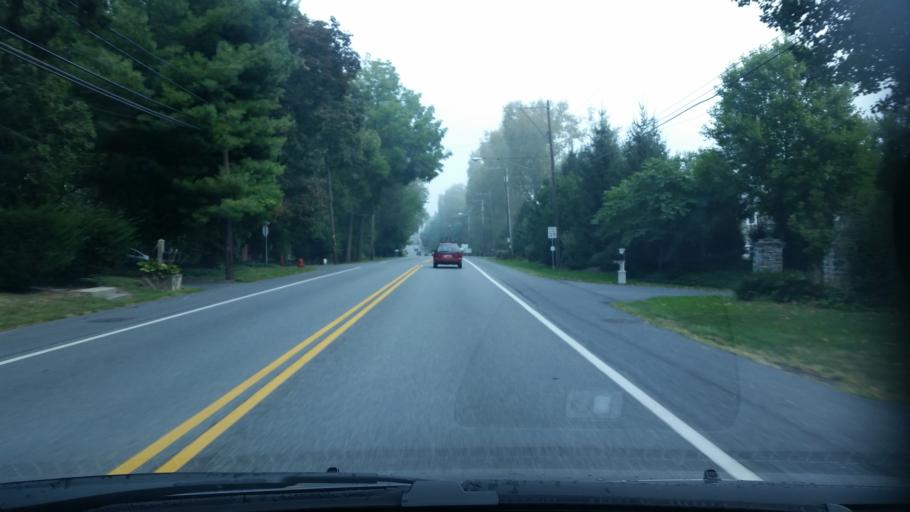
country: US
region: Pennsylvania
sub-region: Lancaster County
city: Lancaster
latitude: 40.0666
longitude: -76.2720
